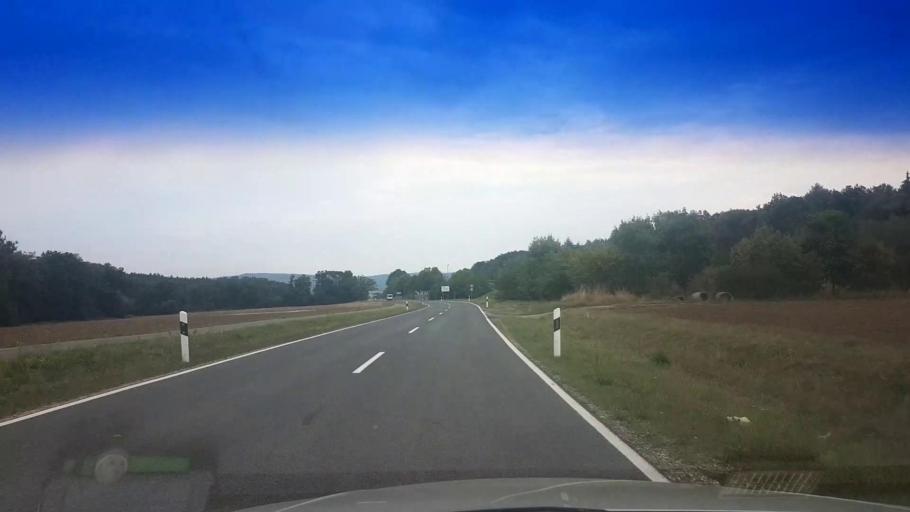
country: DE
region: Bavaria
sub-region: Upper Franconia
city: Memmelsdorf
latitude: 49.9193
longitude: 10.9680
